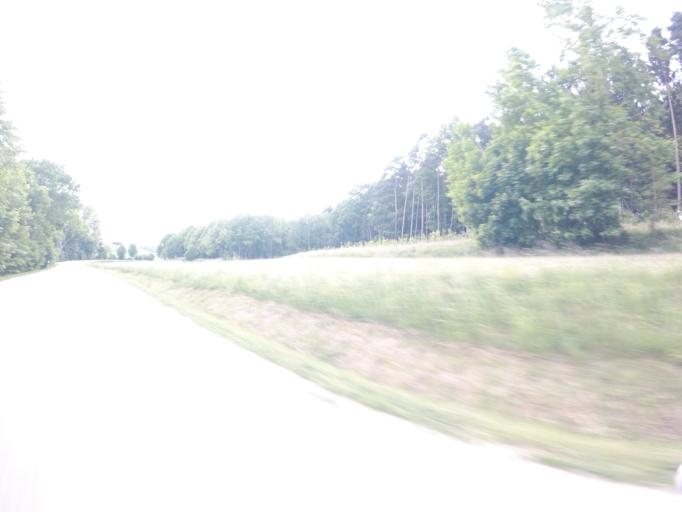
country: DE
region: Bavaria
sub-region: Upper Bavaria
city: Reichertshausen
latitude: 48.4827
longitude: 11.5201
